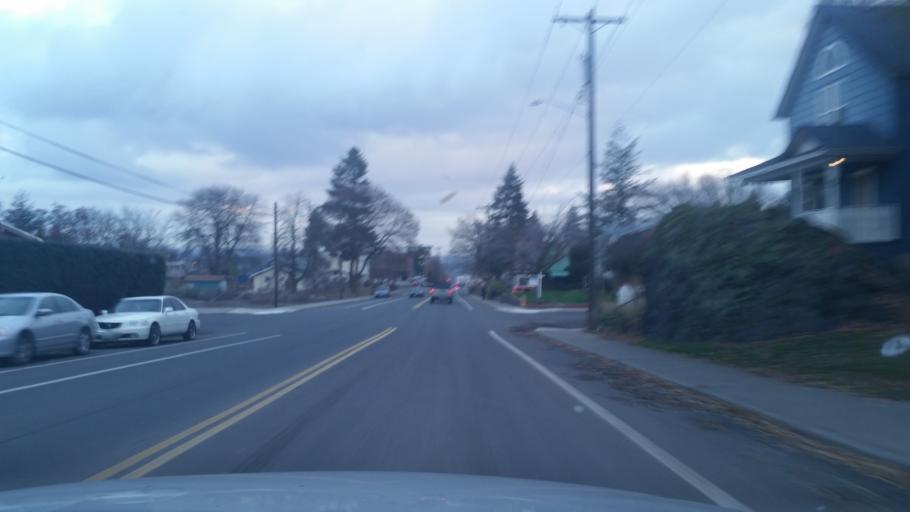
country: US
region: Washington
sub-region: Spokane County
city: Spokane
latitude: 47.6482
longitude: -117.4032
